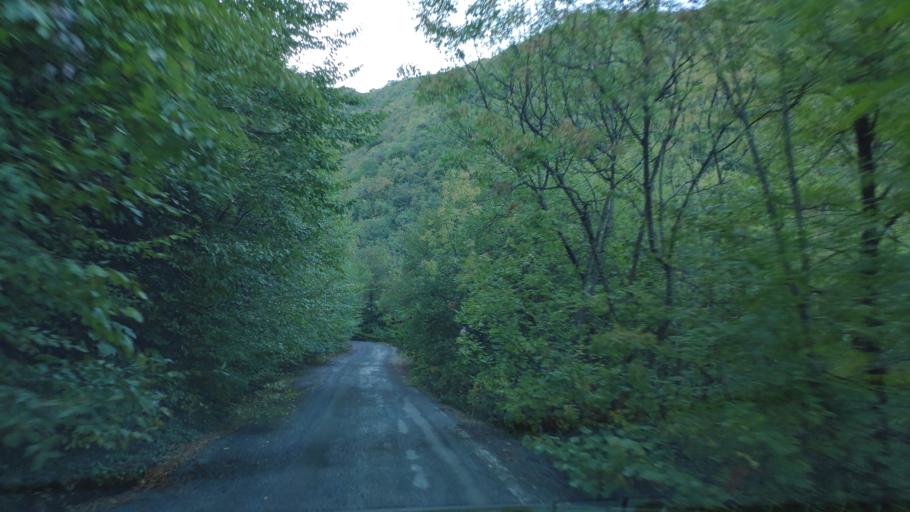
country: GR
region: Peloponnese
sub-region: Nomos Arkadias
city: Dimitsana
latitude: 37.5611
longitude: 22.0425
